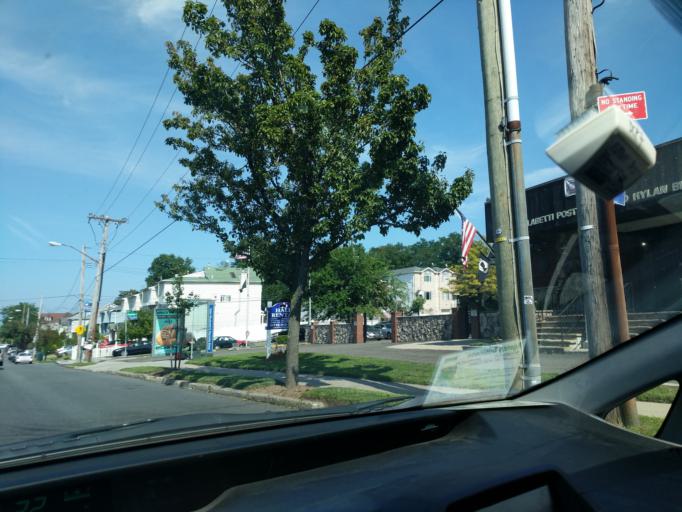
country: US
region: New Jersey
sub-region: Hudson County
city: Bayonne
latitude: 40.6097
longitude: -74.0748
